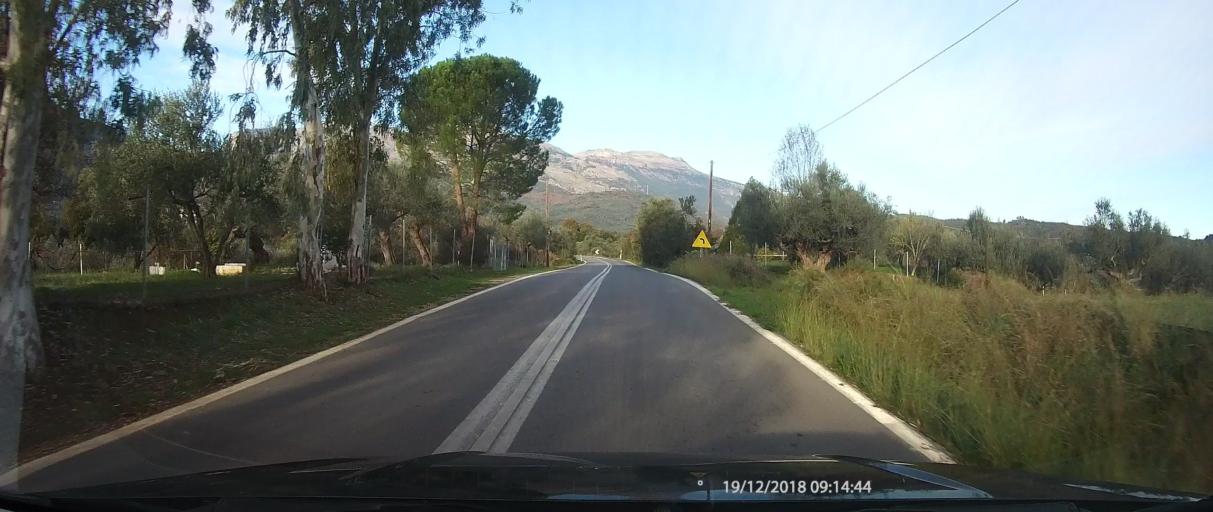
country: GR
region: Peloponnese
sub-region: Nomos Lakonias
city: Magoula
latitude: 37.0882
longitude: 22.3852
